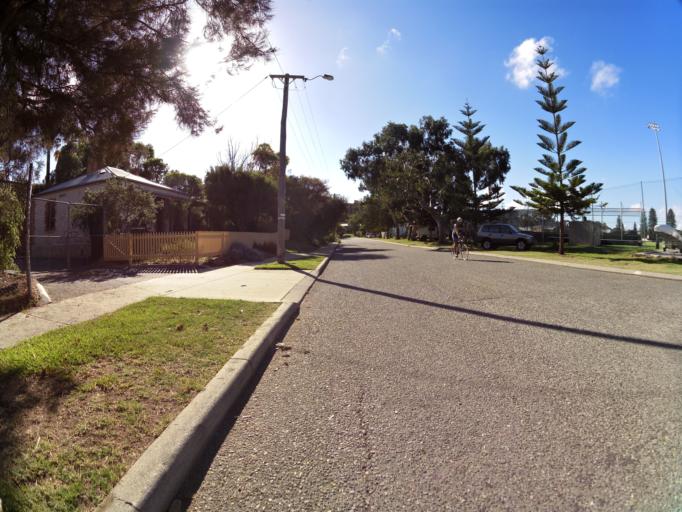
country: AU
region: Western Australia
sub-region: Fremantle
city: North Fremantle
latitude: -32.0364
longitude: 115.7586
